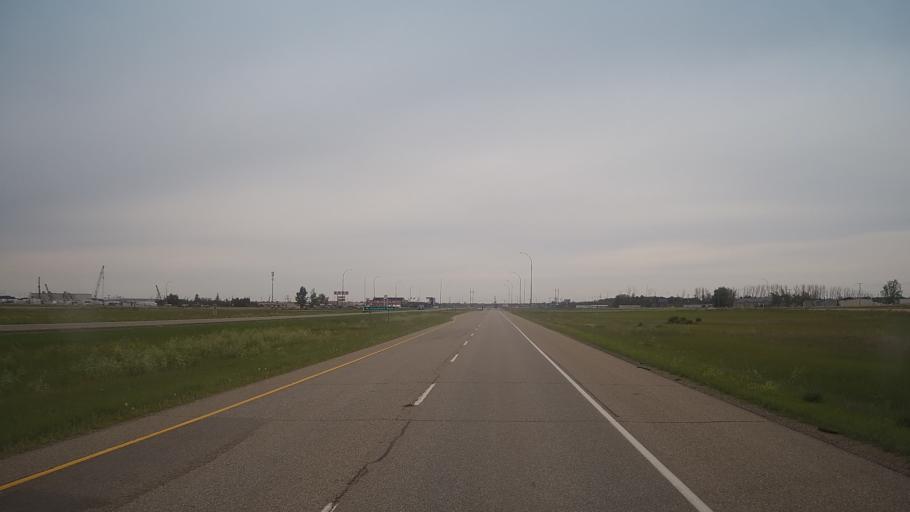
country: CA
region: Saskatchewan
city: Saskatoon
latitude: 52.0510
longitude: -106.5956
